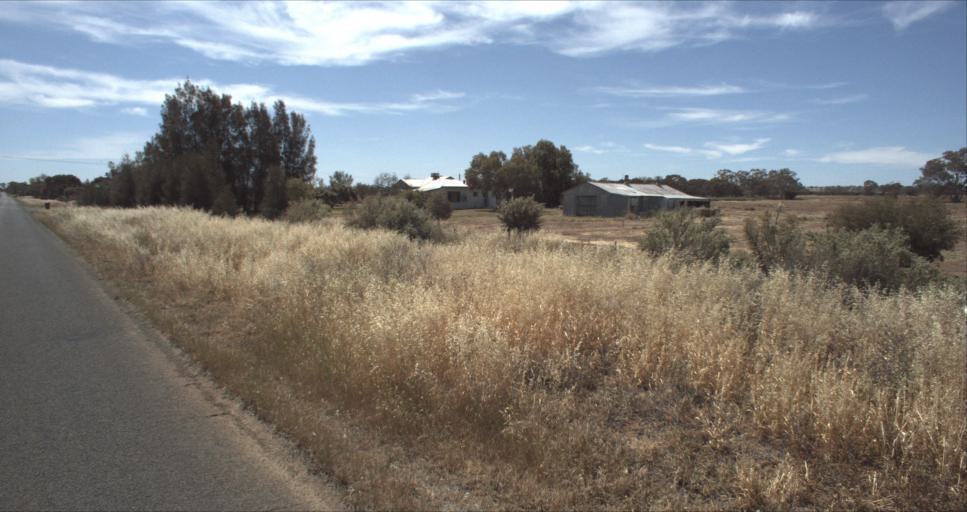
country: AU
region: New South Wales
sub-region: Leeton
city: Leeton
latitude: -34.6071
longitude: 146.4258
